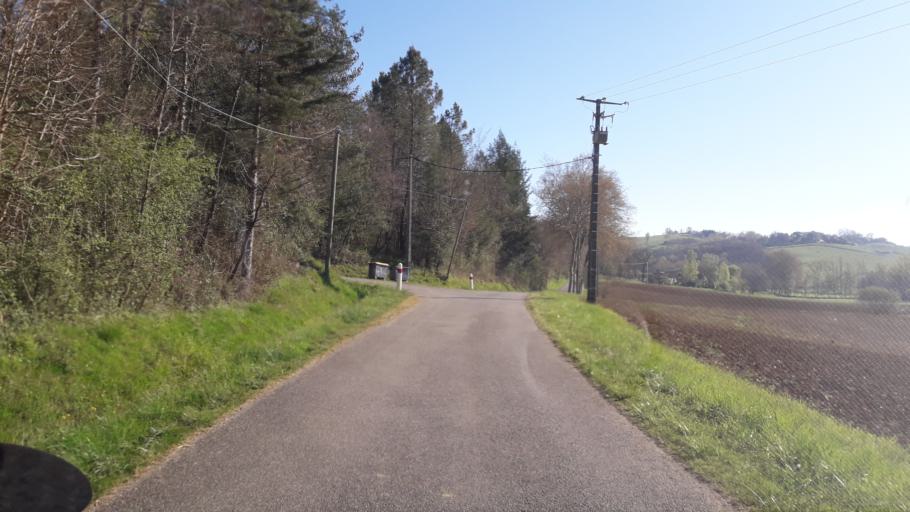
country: FR
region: Midi-Pyrenees
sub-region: Departement de la Haute-Garonne
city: Montesquieu-Volvestre
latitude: 43.1973
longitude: 1.2598
